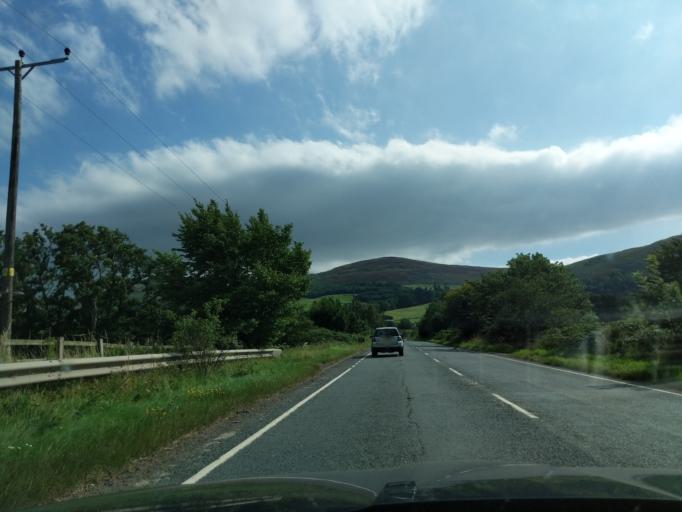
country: GB
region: England
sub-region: Northumberland
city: Wooler
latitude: 55.5657
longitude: -2.0719
